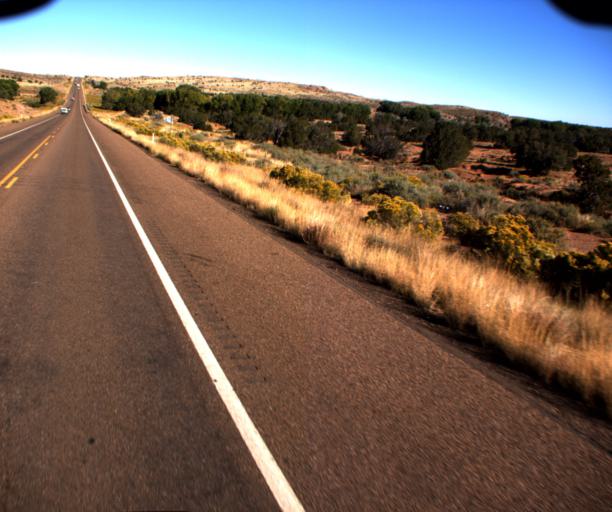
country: US
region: Arizona
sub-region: Navajo County
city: Taylor
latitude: 34.4153
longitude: -110.0831
